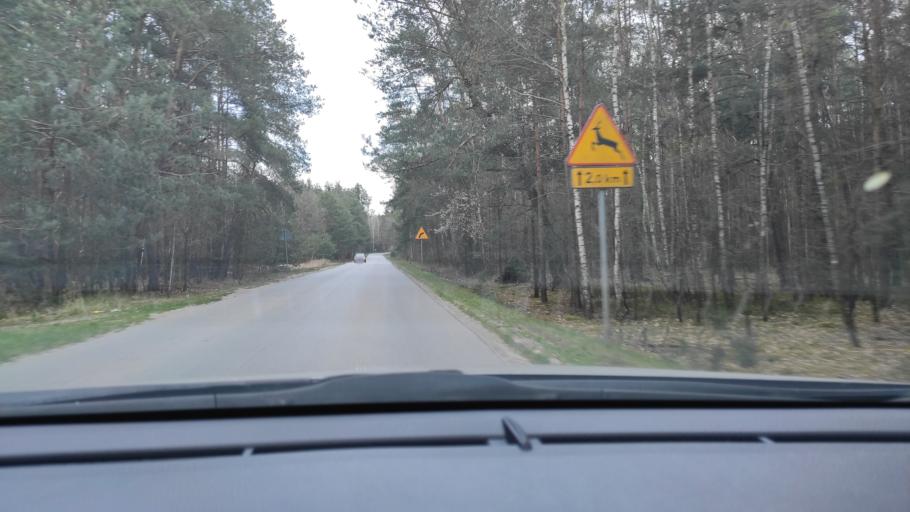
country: PL
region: Masovian Voivodeship
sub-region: Powiat radomski
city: Pionki
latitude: 51.5493
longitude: 21.3707
